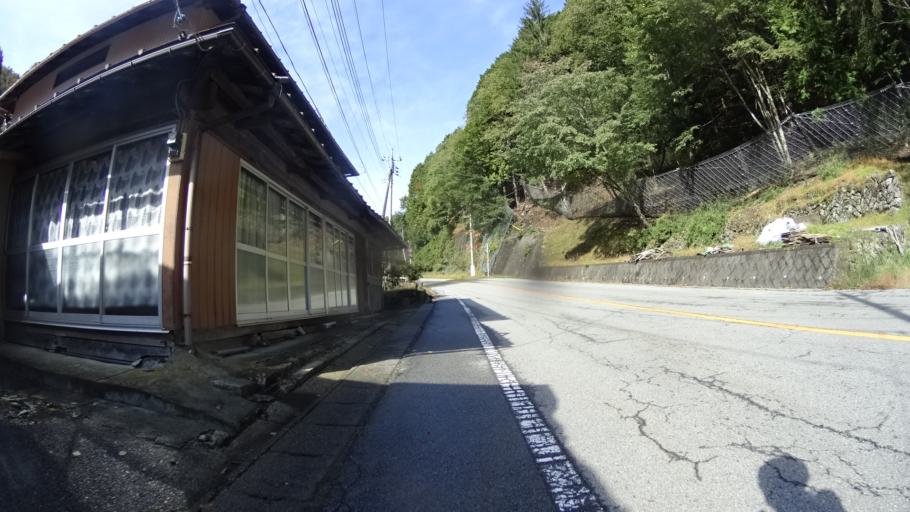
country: JP
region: Yamanashi
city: Enzan
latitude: 35.8058
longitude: 138.8346
